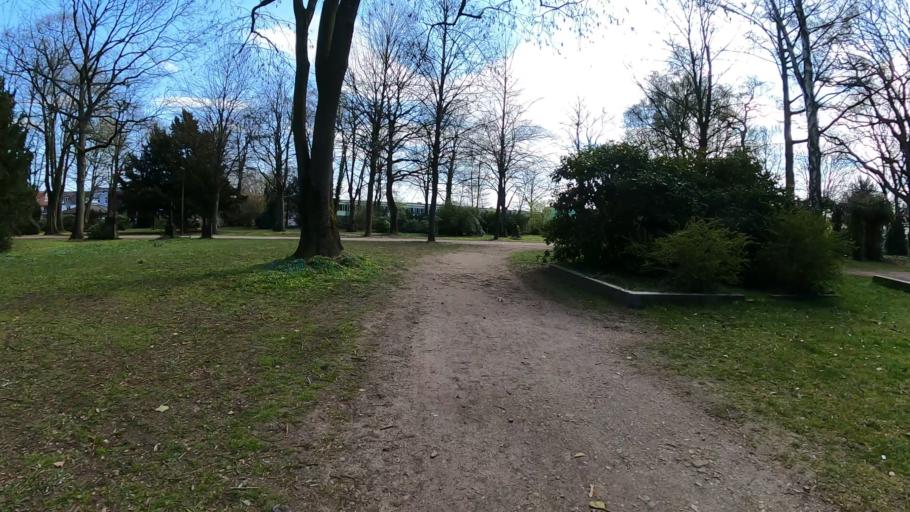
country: DE
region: Hamburg
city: Harburg
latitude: 53.4547
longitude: 9.9798
